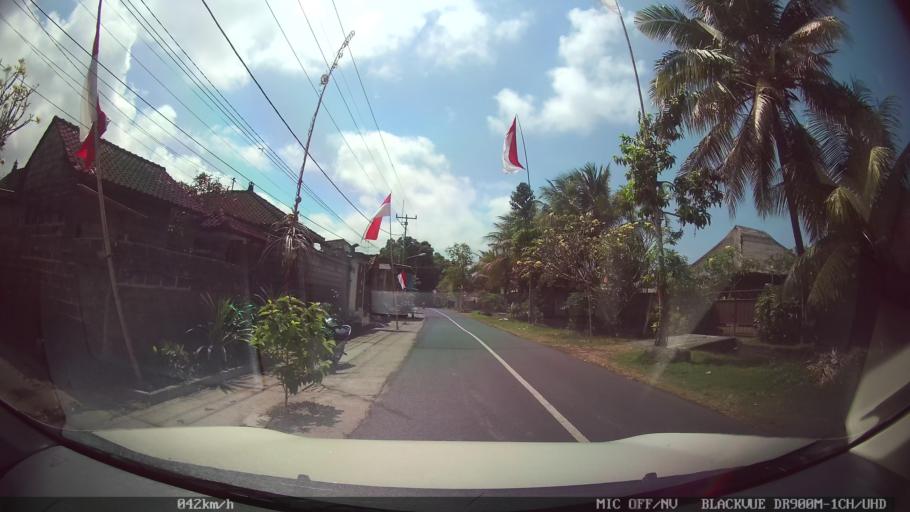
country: ID
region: Bali
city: Banjar Pasekan
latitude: -8.6033
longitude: 115.2965
